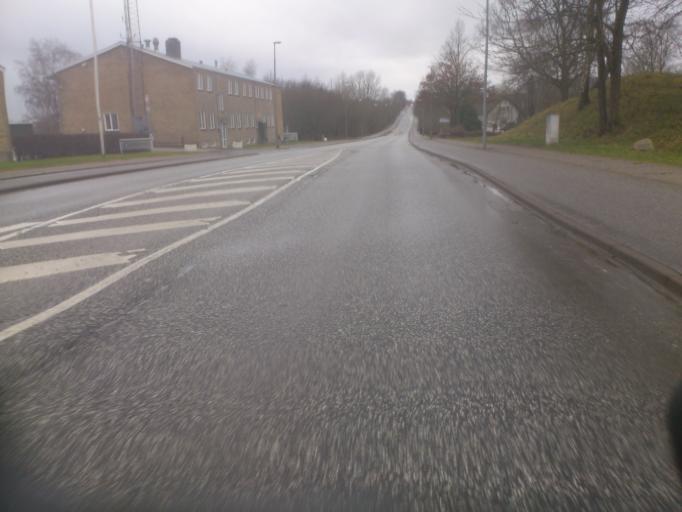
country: DK
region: South Denmark
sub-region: Fredericia Kommune
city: Fredericia
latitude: 55.5640
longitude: 9.7454
